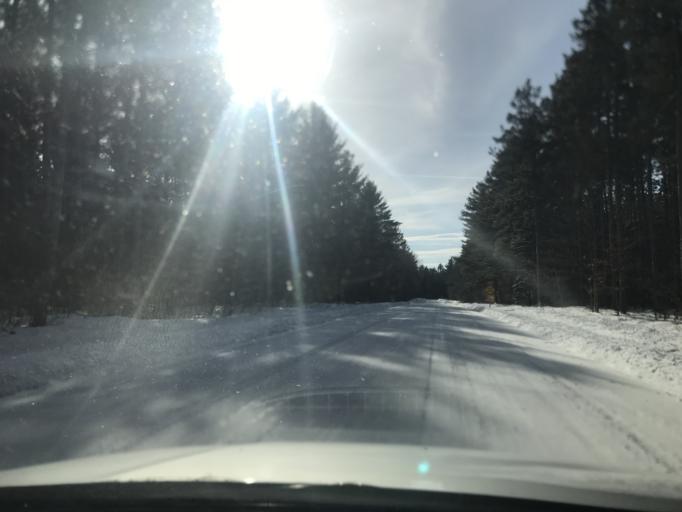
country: US
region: Wisconsin
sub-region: Oconto County
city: Gillett
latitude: 45.1394
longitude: -88.2482
